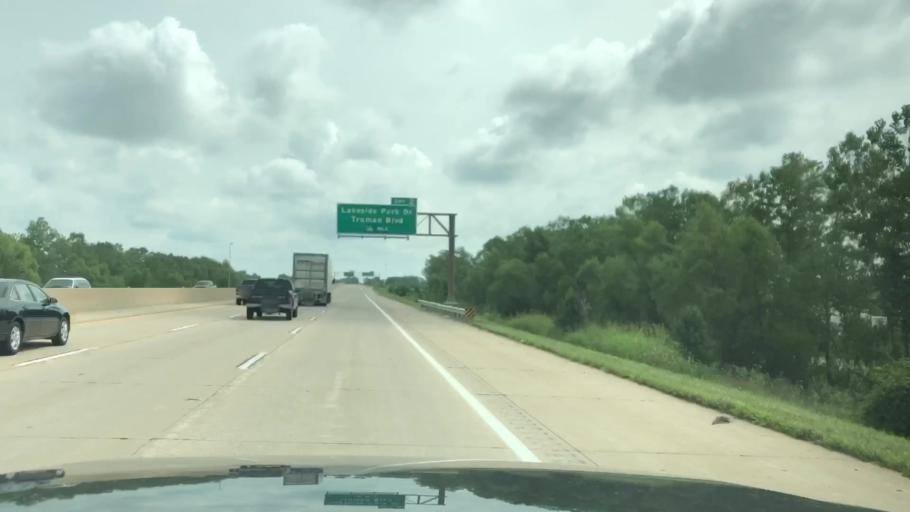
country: US
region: Missouri
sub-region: Saint Charles County
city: Saint Peters
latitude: 38.8161
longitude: -90.5696
